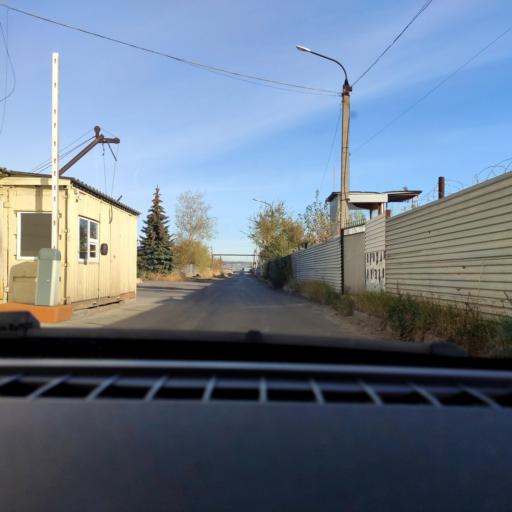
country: RU
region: Voronezj
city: Somovo
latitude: 51.6711
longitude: 39.2991
